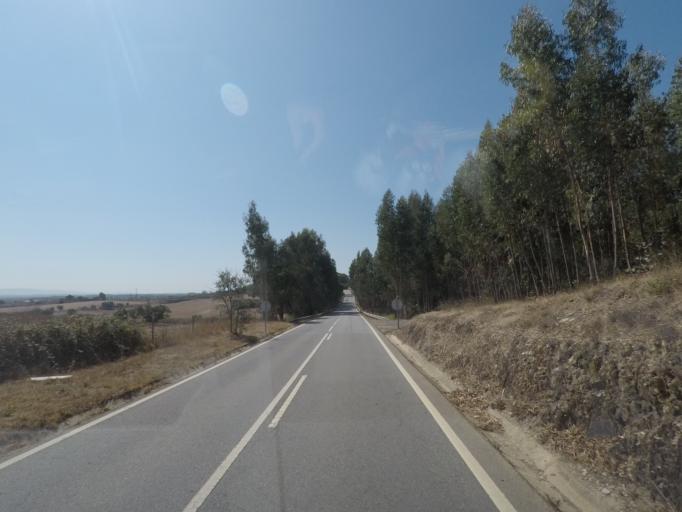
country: PT
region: Beja
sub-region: Odemira
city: Sao Teotonio
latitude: 37.5401
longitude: -8.6896
